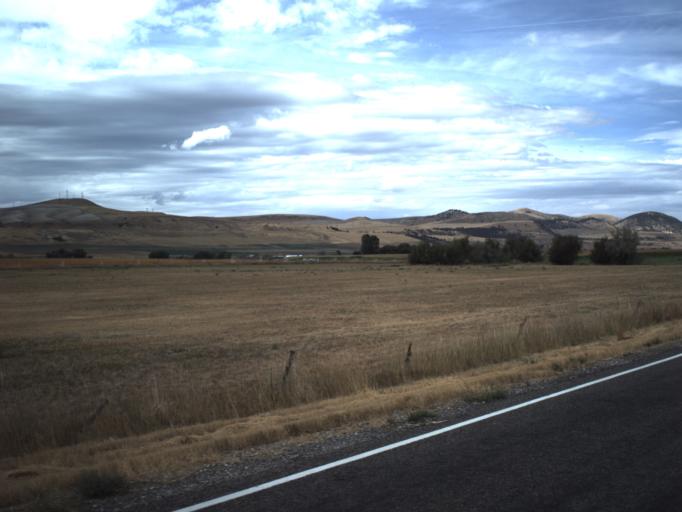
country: US
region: Utah
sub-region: Cache County
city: Lewiston
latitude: 41.9250
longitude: -111.9531
